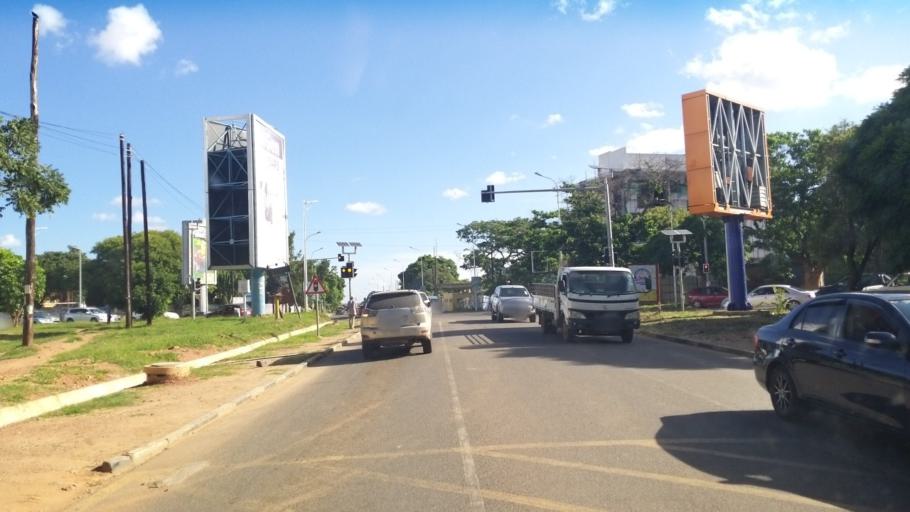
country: ZM
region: Lusaka
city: Lusaka
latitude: -15.4245
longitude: 28.3120
